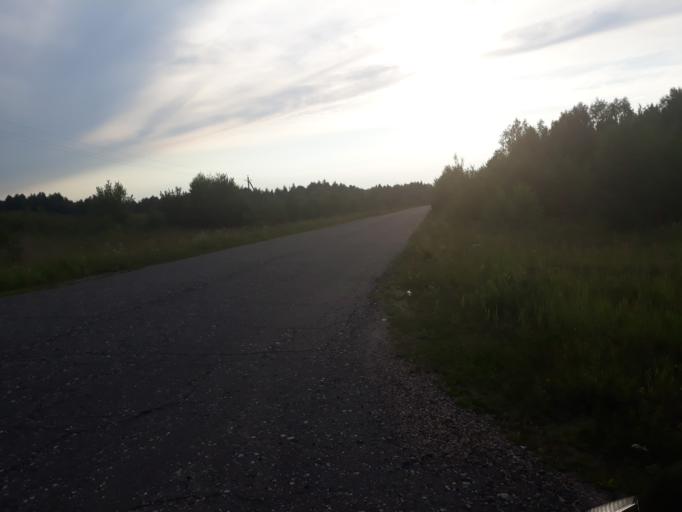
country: RU
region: Jaroslavl
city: Petrovsk
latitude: 56.8738
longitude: 39.0877
